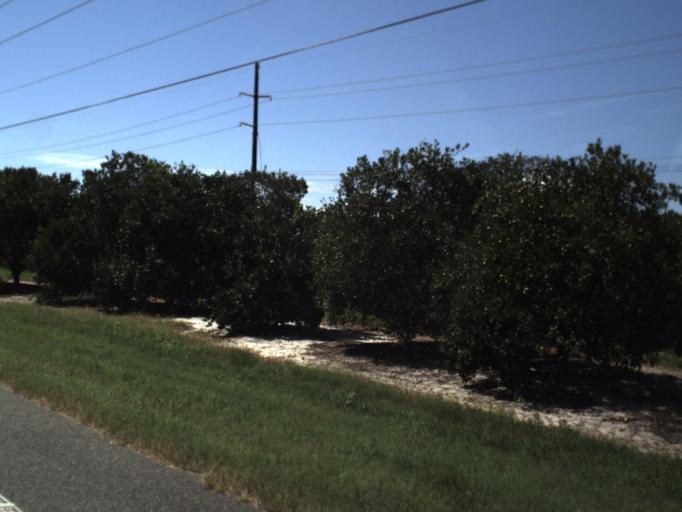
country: US
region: Florida
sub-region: Polk County
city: Lake Wales
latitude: 27.9409
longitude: -81.6001
